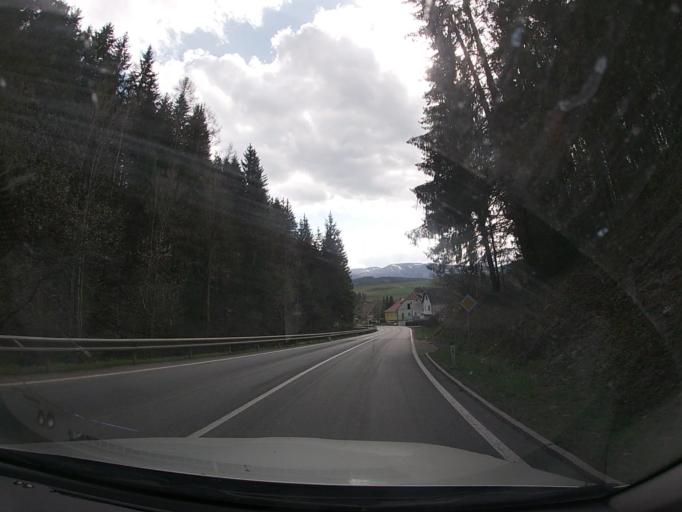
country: AT
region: Styria
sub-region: Politischer Bezirk Murau
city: Neumarkt in Steiermark
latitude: 47.0827
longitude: 14.4284
